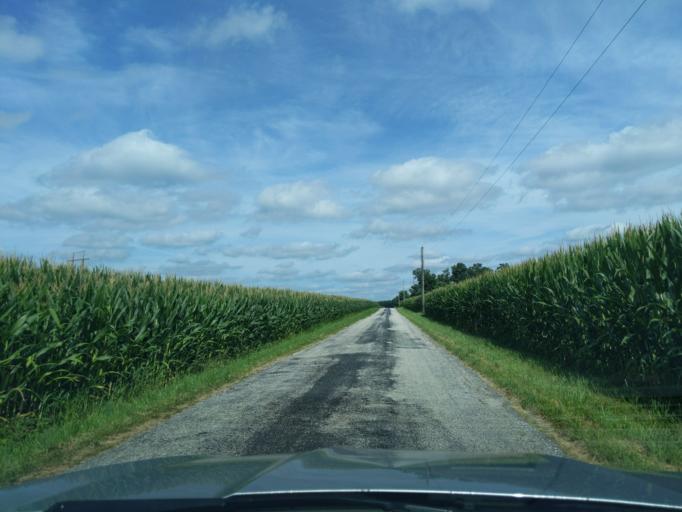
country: US
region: Indiana
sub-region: Ripley County
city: Osgood
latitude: 39.2352
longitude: -85.3734
